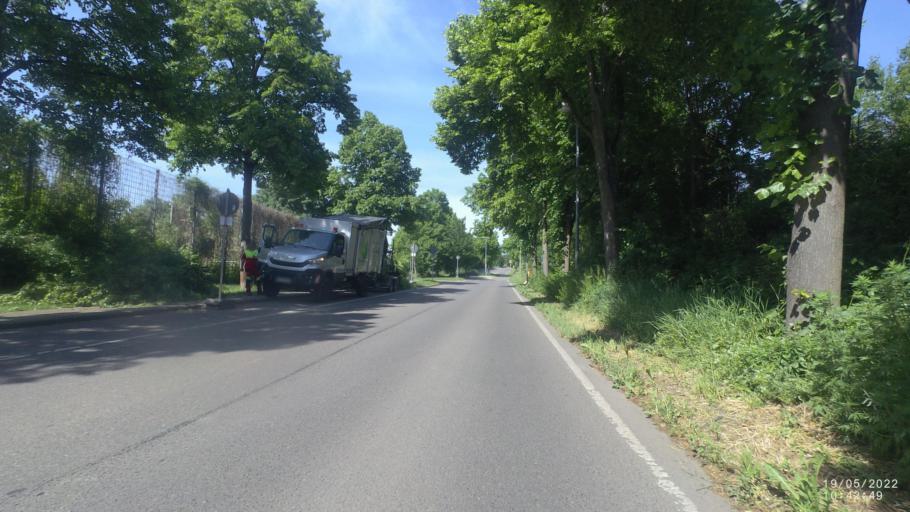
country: DE
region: Baden-Wuerttemberg
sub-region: Regierungsbezirk Stuttgart
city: Stuttgart Muehlhausen
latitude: 48.8384
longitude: 9.2578
